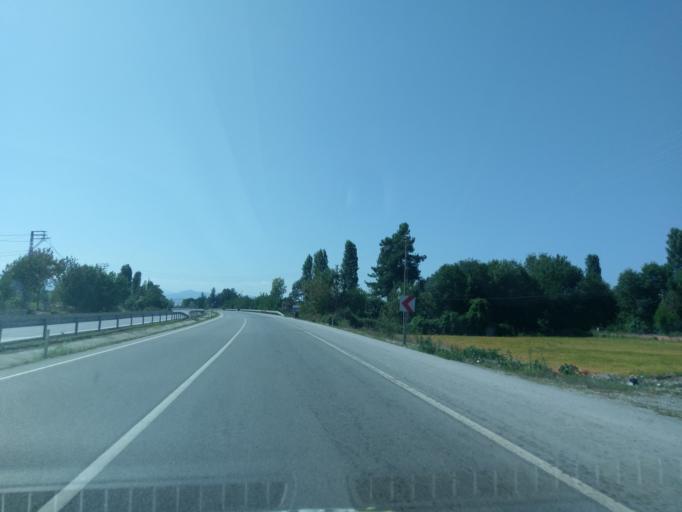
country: TR
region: Samsun
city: Alacam
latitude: 41.6125
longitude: 35.7084
